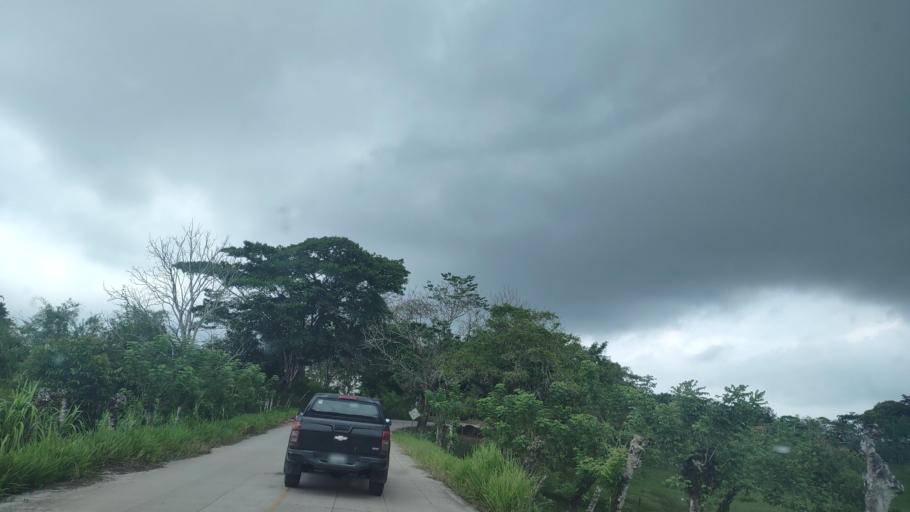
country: MX
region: Veracruz
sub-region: Uxpanapa
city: Poblado 10
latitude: 17.4948
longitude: -94.1715
